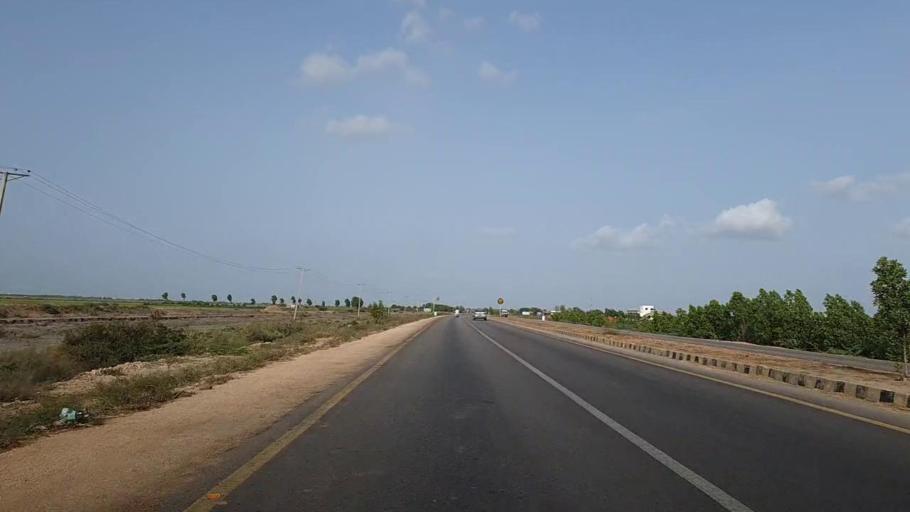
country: PK
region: Sindh
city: Thatta
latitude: 24.7451
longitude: 67.8534
